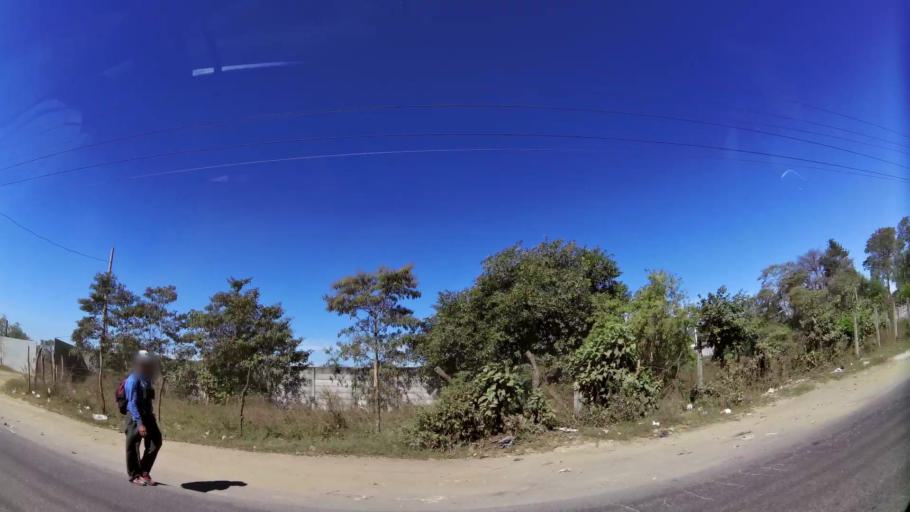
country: SV
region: La Libertad
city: San Juan Opico
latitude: 13.7982
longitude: -89.3655
